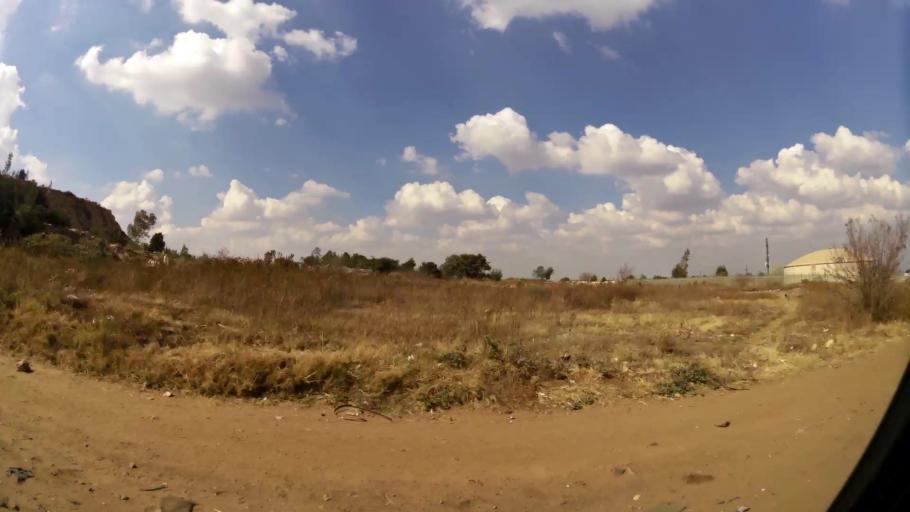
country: ZA
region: Gauteng
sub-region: City of Johannesburg Metropolitan Municipality
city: Roodepoort
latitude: -26.1885
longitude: 27.8678
